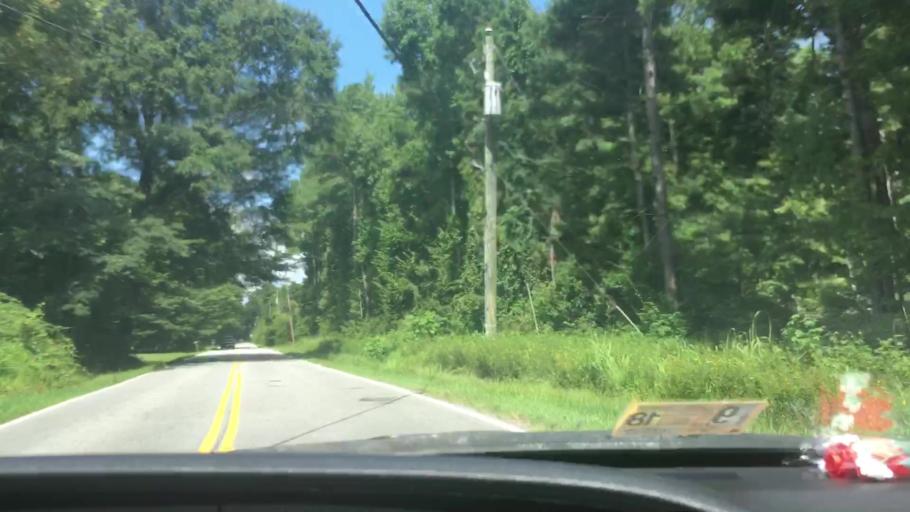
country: US
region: Virginia
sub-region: City of Virginia Beach
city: Virginia Beach
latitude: 36.7365
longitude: -76.1008
